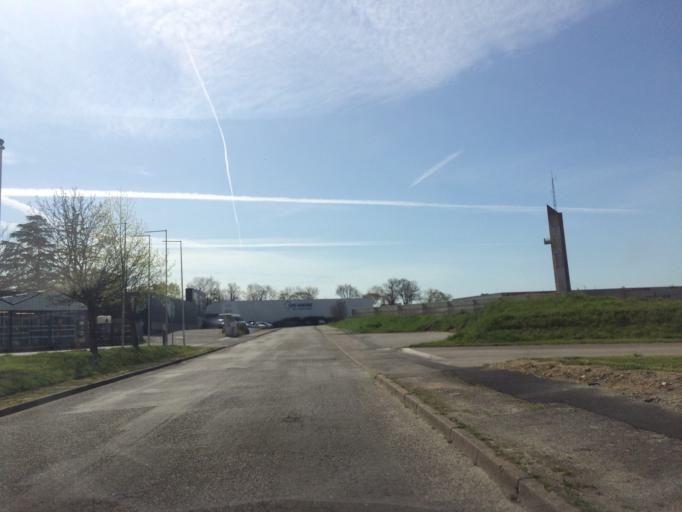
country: FR
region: Brittany
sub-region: Departement d'Ille-et-Vilaine
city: Redon
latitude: 47.6620
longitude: -2.0692
